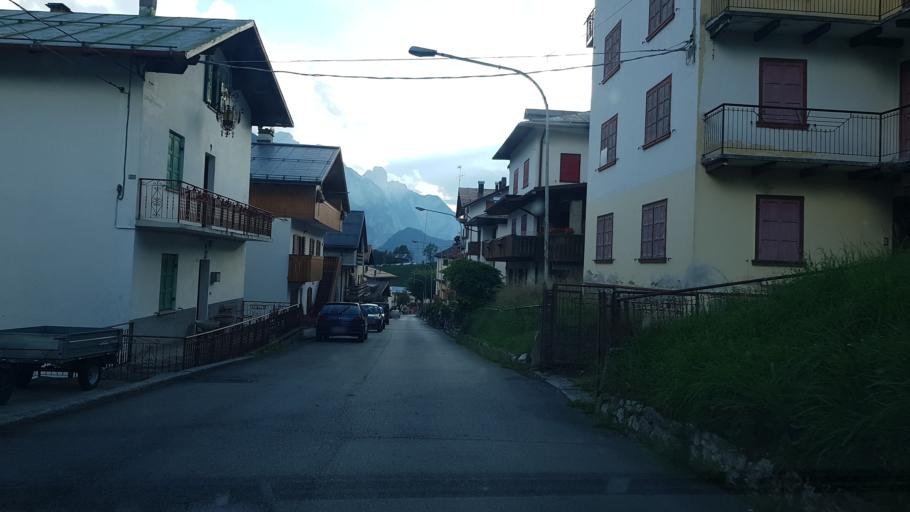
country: IT
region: Veneto
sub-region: Provincia di Belluno
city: San Pietro di Cadore
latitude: 46.5724
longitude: 12.5881
